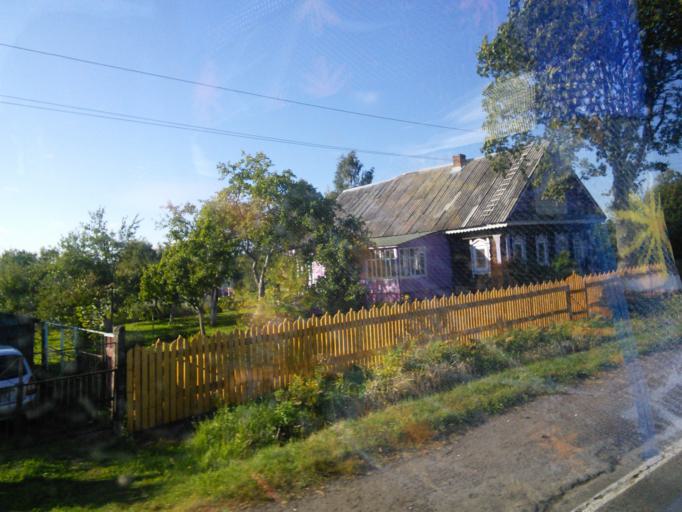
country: RU
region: Jaroslavl
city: Rybinsk
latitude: 58.2639
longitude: 38.8510
